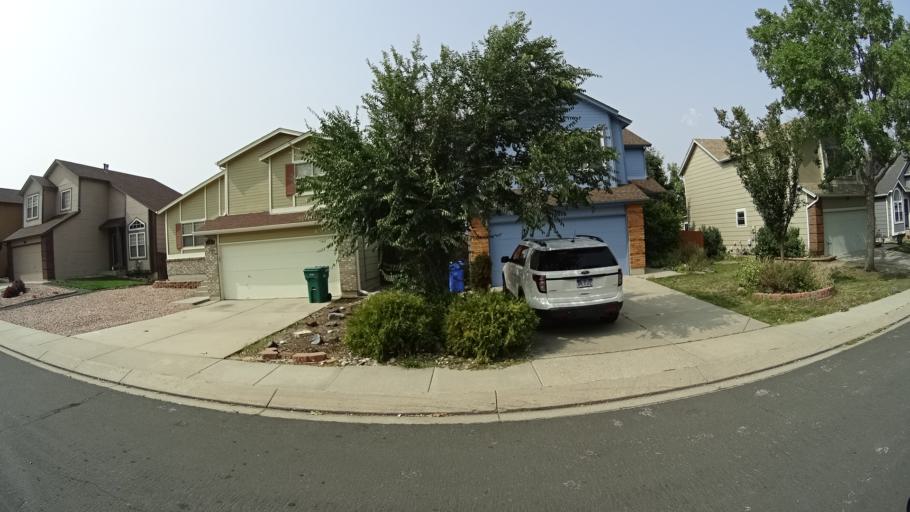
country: US
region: Colorado
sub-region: El Paso County
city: Cimarron Hills
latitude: 38.9181
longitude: -104.7283
